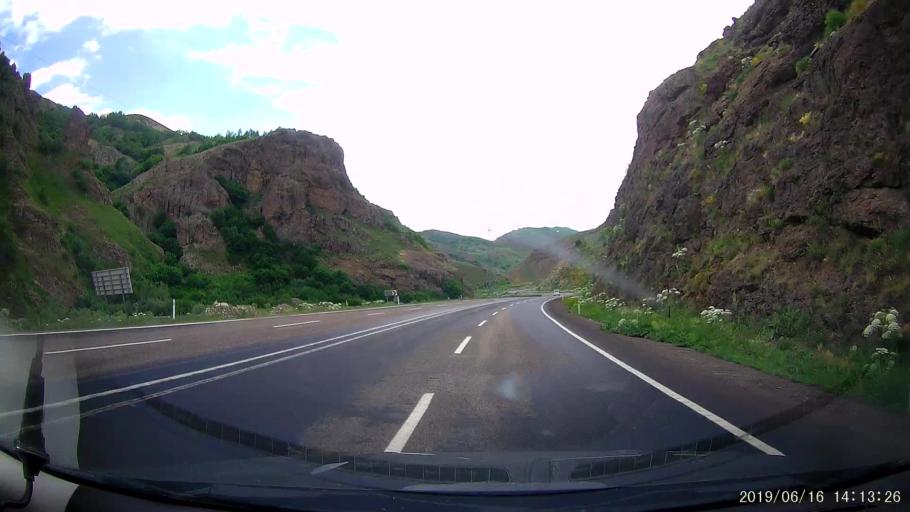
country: TR
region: Agri
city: Tahir
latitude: 39.7968
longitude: 42.5167
